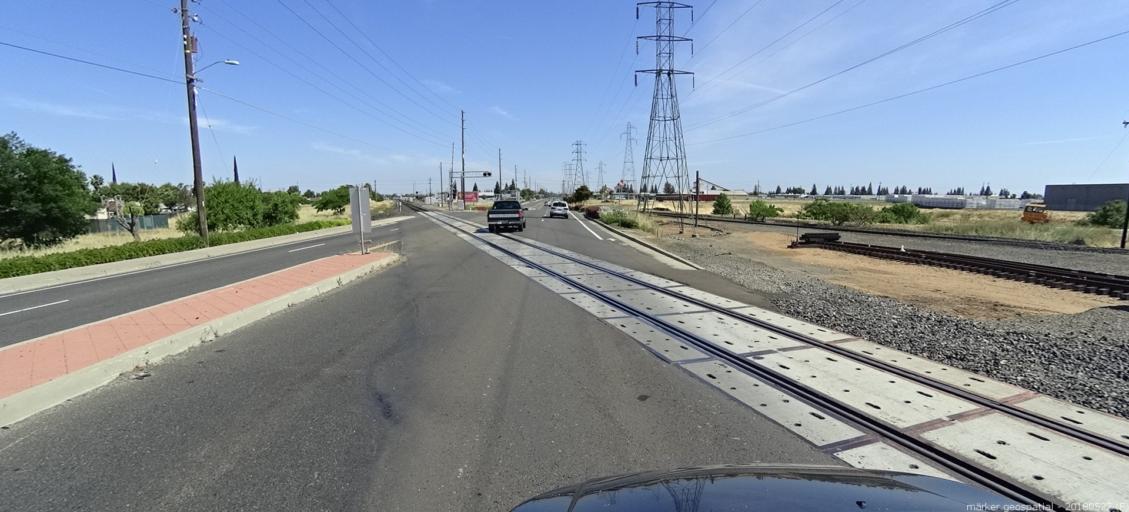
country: US
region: California
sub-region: Sacramento County
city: Florin
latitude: 38.5290
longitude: -121.4092
